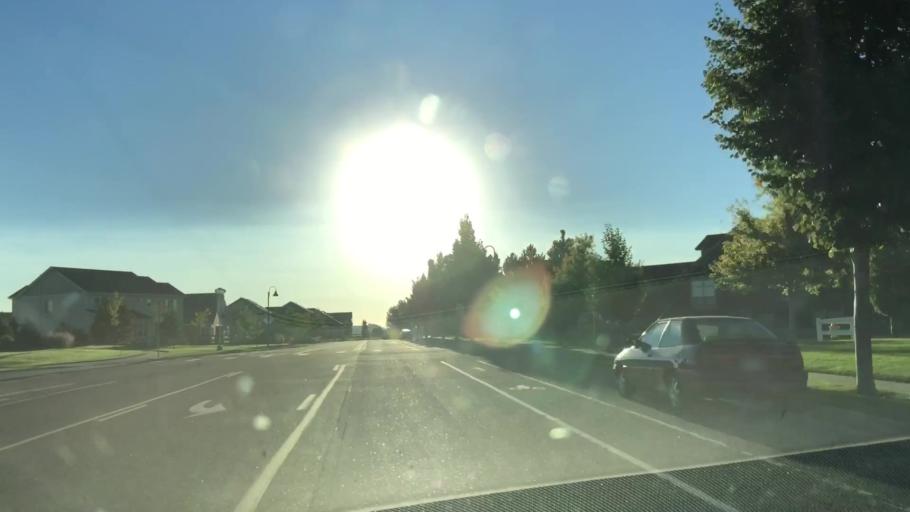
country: US
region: Colorado
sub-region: Larimer County
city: Loveland
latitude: 40.4144
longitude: -105.0186
